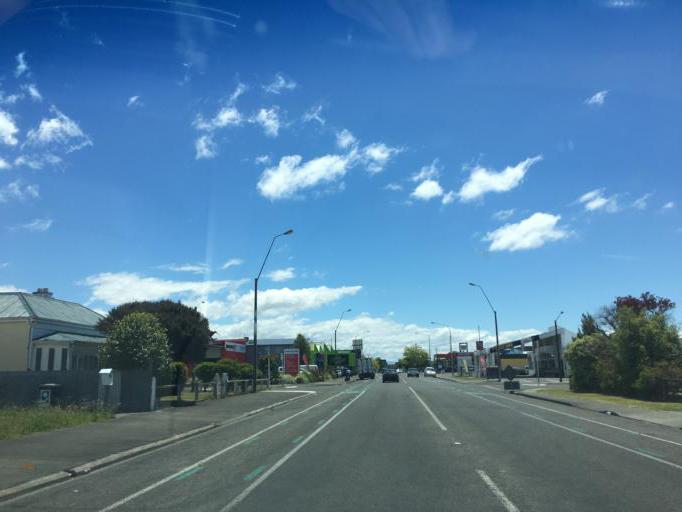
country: NZ
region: Hawke's Bay
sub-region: Hastings District
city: Hastings
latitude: -39.6440
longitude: 176.8509
